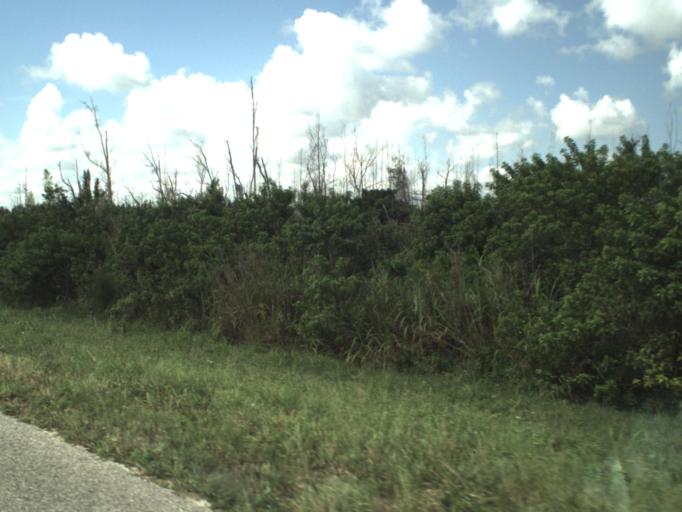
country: US
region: Florida
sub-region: Broward County
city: Weston
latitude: 26.0469
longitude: -80.4340
